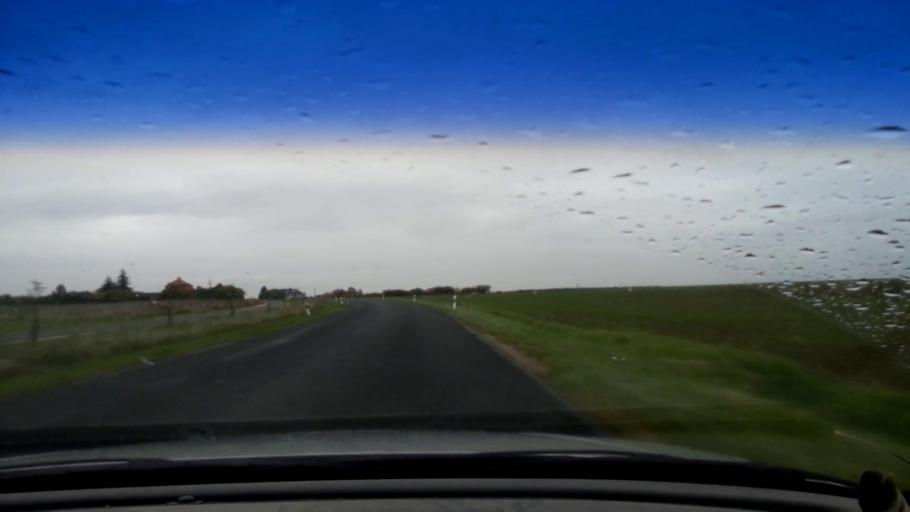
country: DE
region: Bavaria
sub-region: Upper Franconia
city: Priesendorf
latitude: 49.8750
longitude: 10.7122
